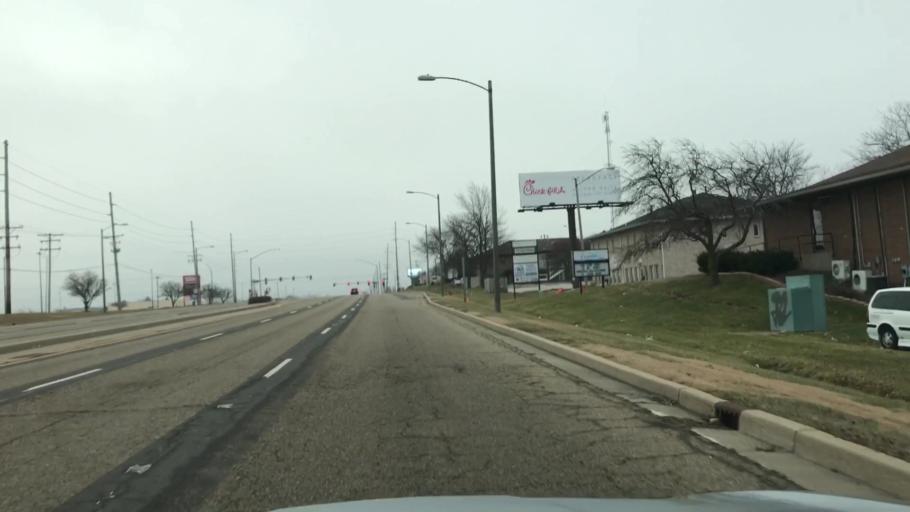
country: US
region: Illinois
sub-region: McLean County
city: Normal
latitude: 40.5130
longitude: -88.9535
